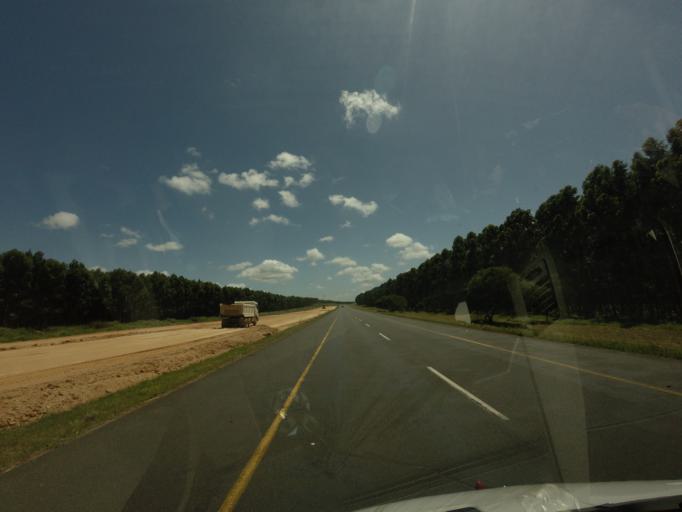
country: ZA
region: KwaZulu-Natal
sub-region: uThungulu District Municipality
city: Empangeni
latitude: -28.7440
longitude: 31.9380
